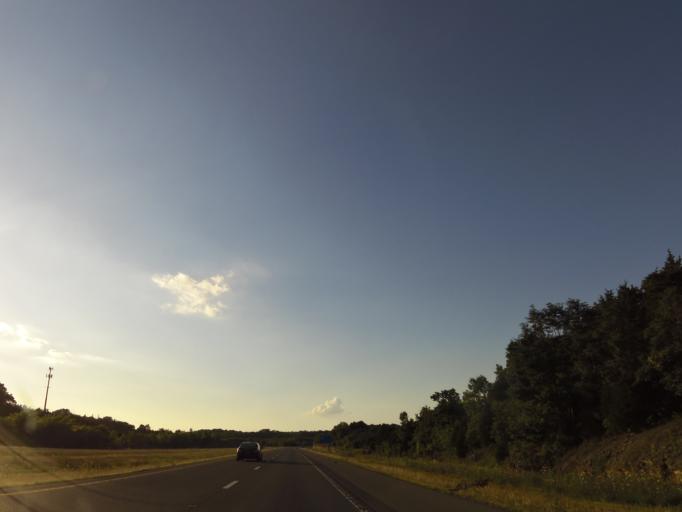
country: US
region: Tennessee
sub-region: Rutherford County
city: Smyrna
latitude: 35.9614
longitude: -86.4465
